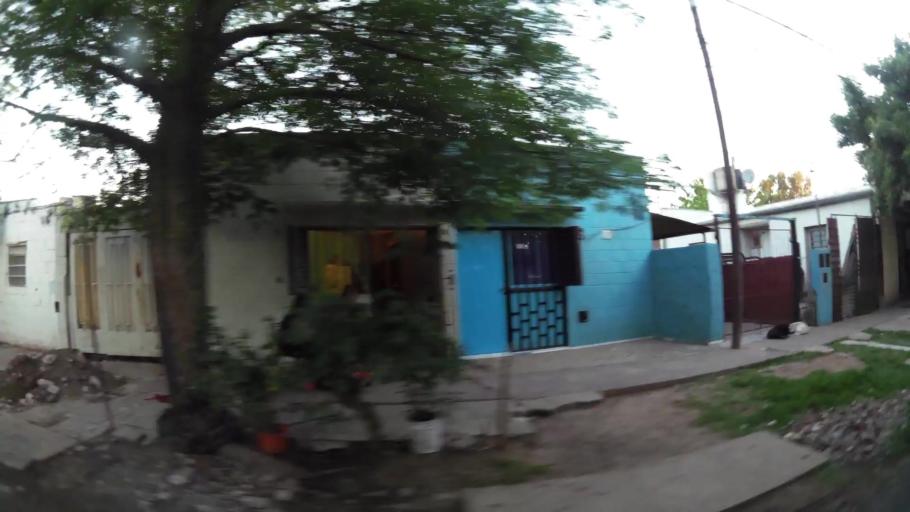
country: AR
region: Santa Fe
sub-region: Departamento de Rosario
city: Rosario
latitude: -32.9656
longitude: -60.6907
